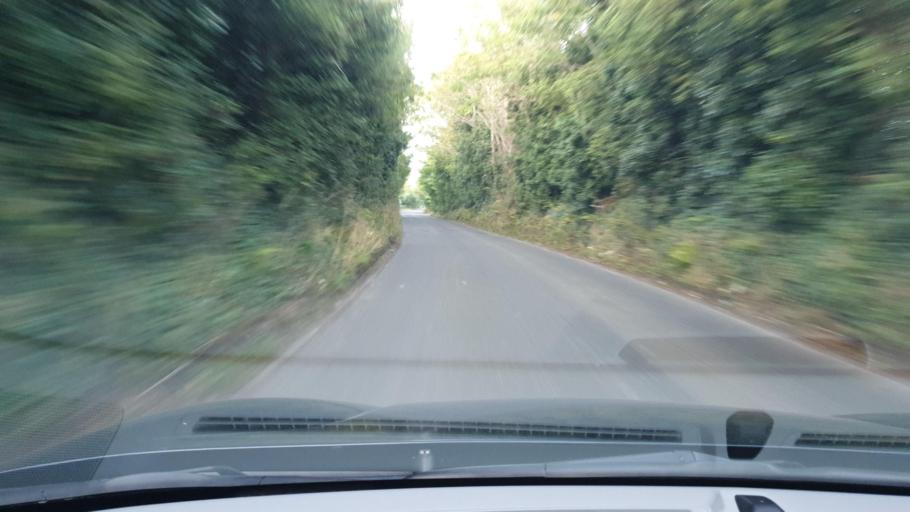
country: IE
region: Leinster
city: Balrothery
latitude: 53.5615
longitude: -6.2219
